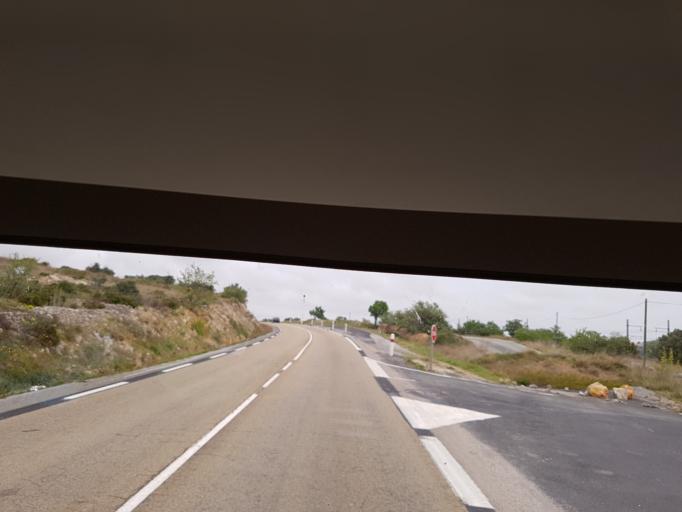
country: FR
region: Languedoc-Roussillon
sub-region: Departement de l'Aude
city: Leucate
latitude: 42.9005
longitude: 2.9998
